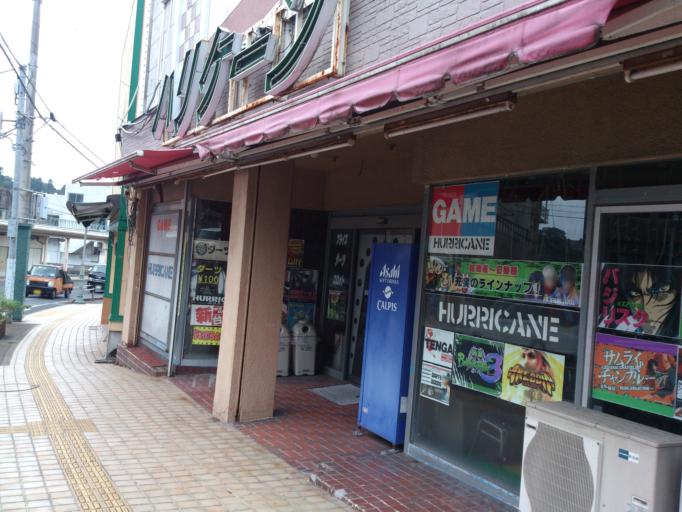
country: JP
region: Kagoshima
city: Kanoya
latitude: 31.3862
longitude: 130.8532
